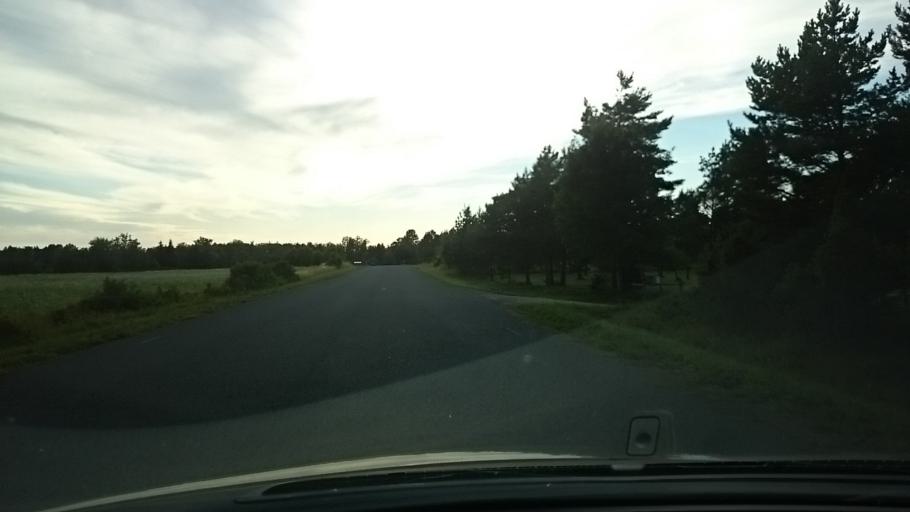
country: EE
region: Saare
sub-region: Kuressaare linn
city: Kuressaare
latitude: 58.4191
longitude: 22.1589
